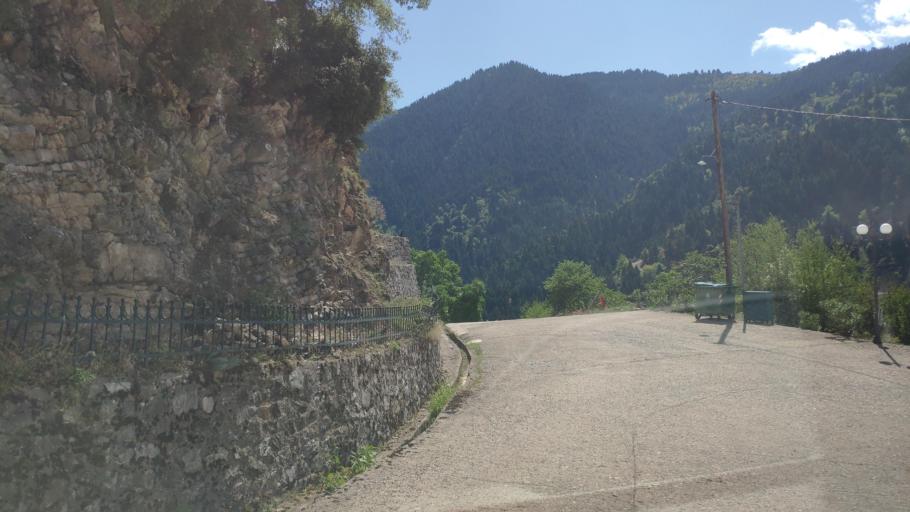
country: GR
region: Central Greece
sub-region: Nomos Evrytanias
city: Kerasochori
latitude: 39.1349
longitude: 21.6508
